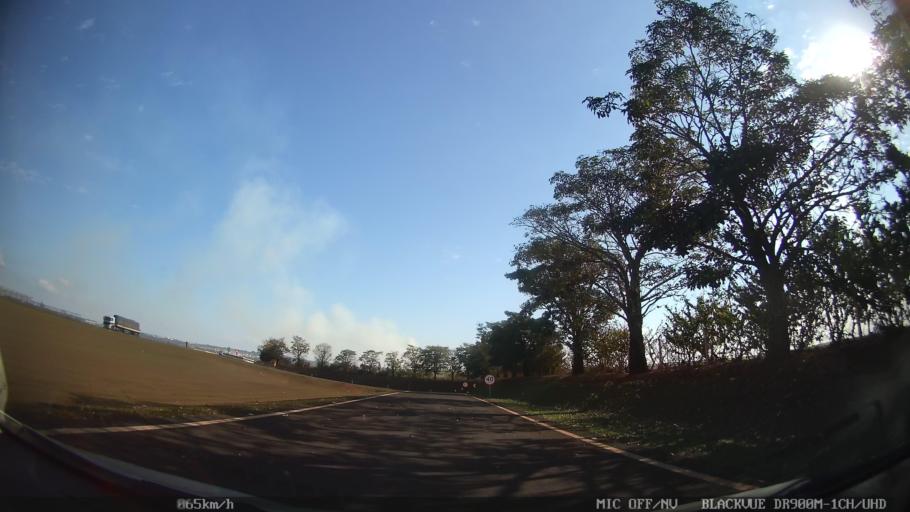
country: BR
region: Sao Paulo
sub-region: Piracicaba
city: Piracicaba
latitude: -22.6771
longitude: -47.5646
